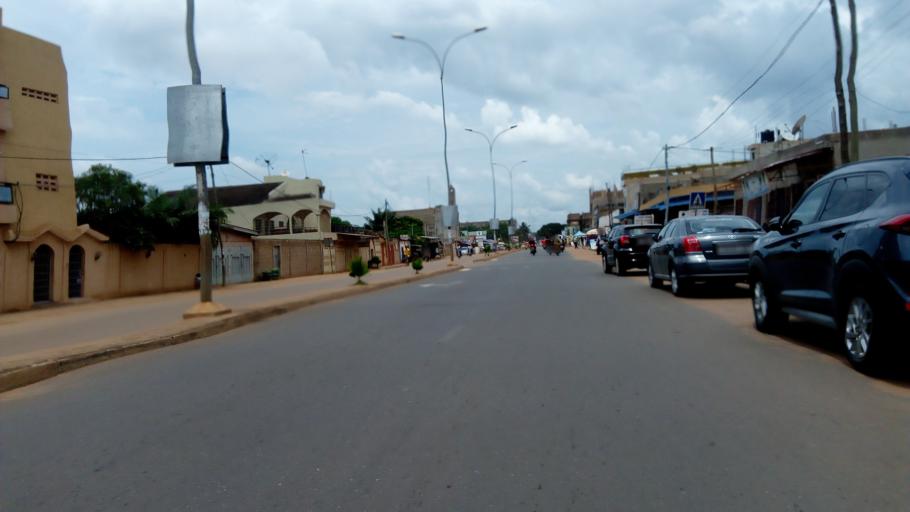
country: TG
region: Maritime
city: Lome
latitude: 6.2172
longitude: 1.1706
